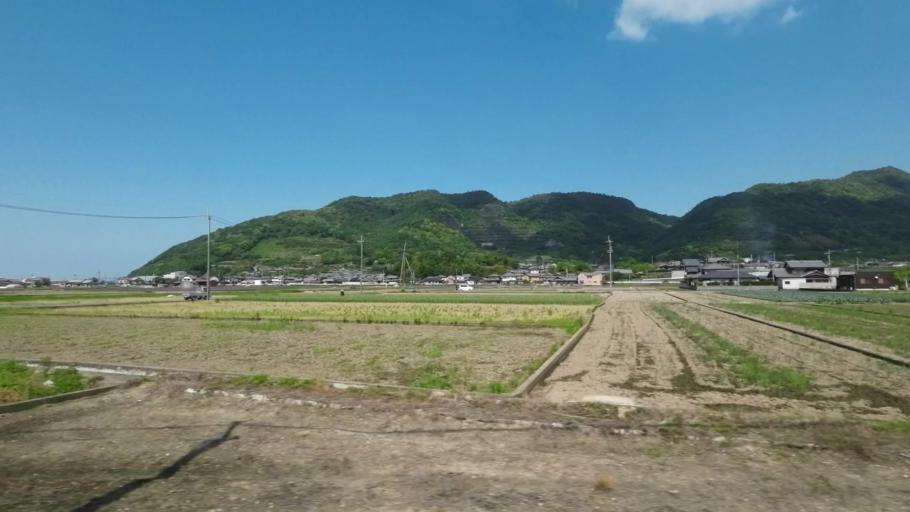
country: JP
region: Kagawa
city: Kan'onjicho
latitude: 34.1442
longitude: 133.6859
